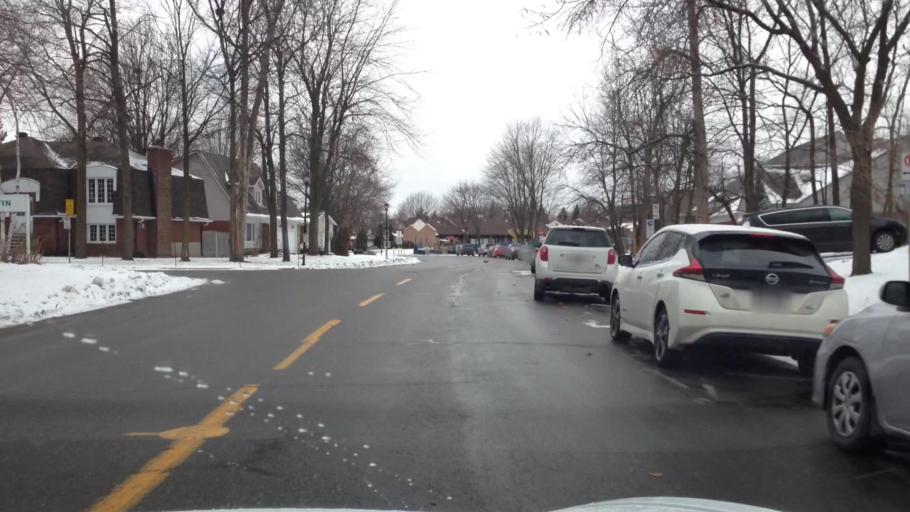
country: CA
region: Quebec
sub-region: Montreal
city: Pointe-Claire
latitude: 45.4473
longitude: -73.8362
